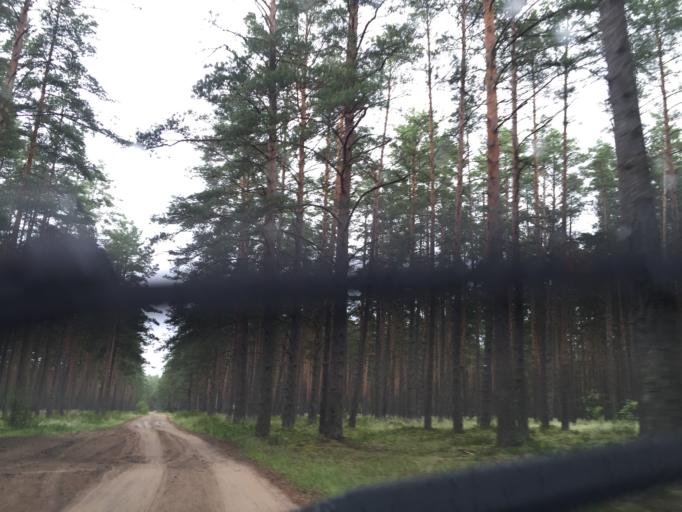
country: LV
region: Riga
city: Jaunciems
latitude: 57.0502
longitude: 24.2063
